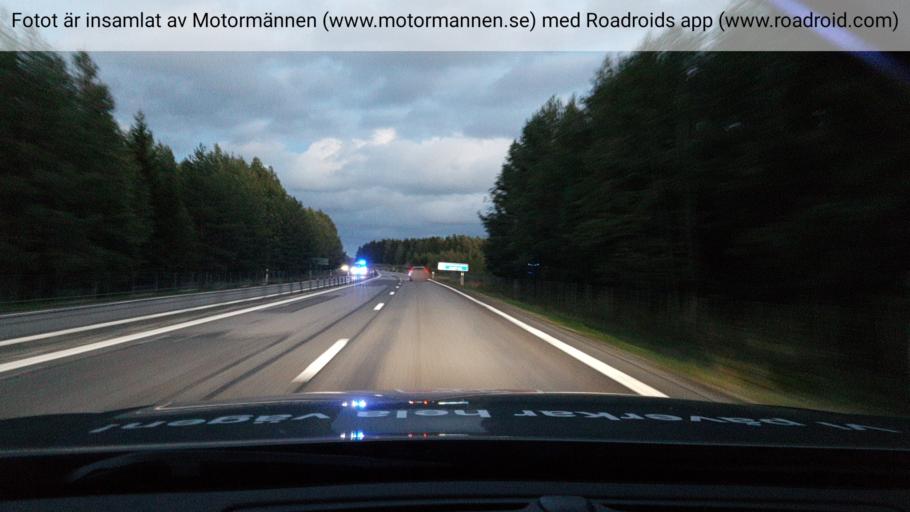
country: SE
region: Vaermland
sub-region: Kristinehamns Kommun
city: Kristinehamn
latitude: 59.3827
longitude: 13.8817
